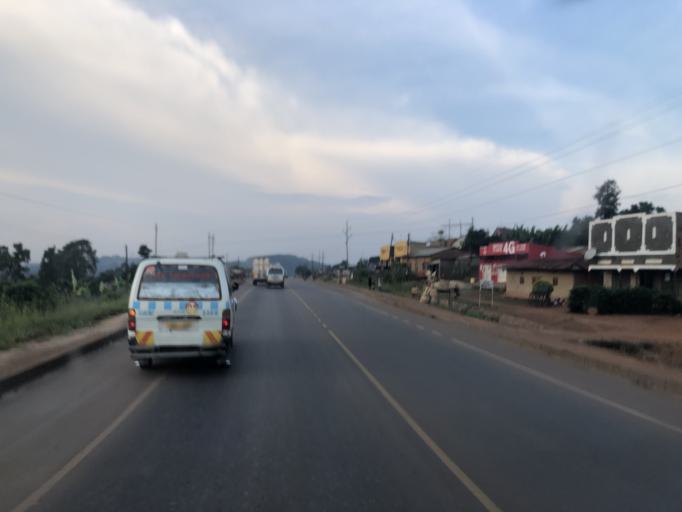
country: UG
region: Central Region
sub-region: Mpigi District
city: Mpigi
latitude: 0.2351
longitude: 32.3472
